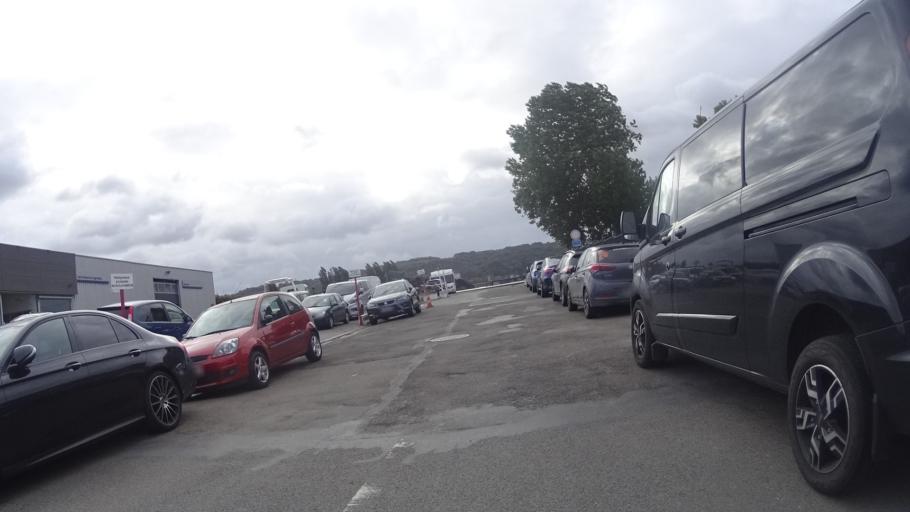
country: BE
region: Wallonia
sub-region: Province de Liege
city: Herstal
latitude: 50.6629
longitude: 5.6332
